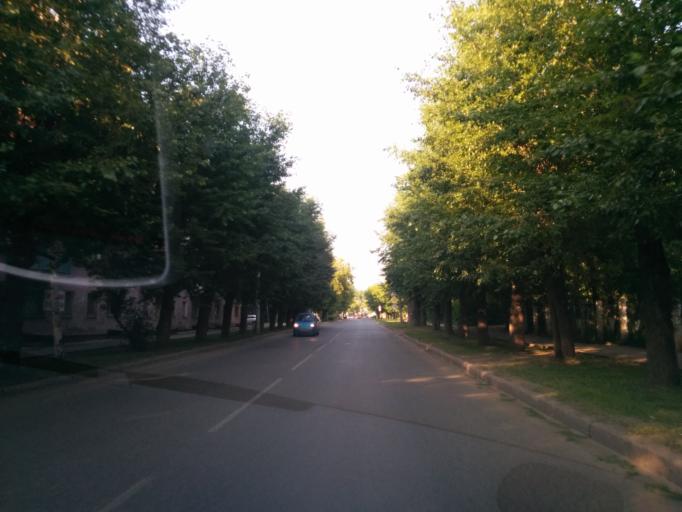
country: RU
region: Perm
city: Perm
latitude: 58.0172
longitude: 56.2838
